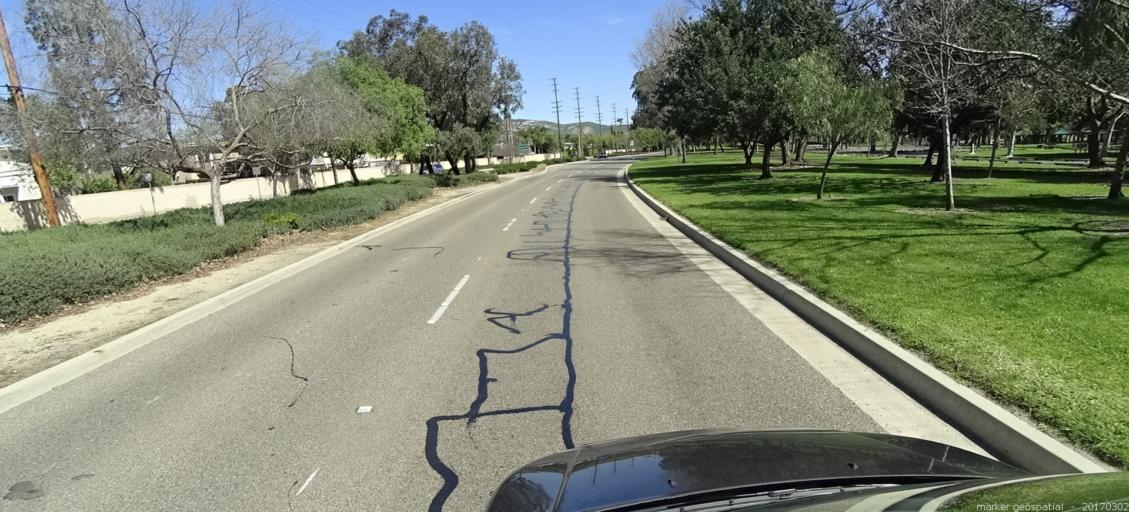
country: US
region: California
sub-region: Orange County
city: Yorba Linda
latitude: 33.8697
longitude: -117.7699
